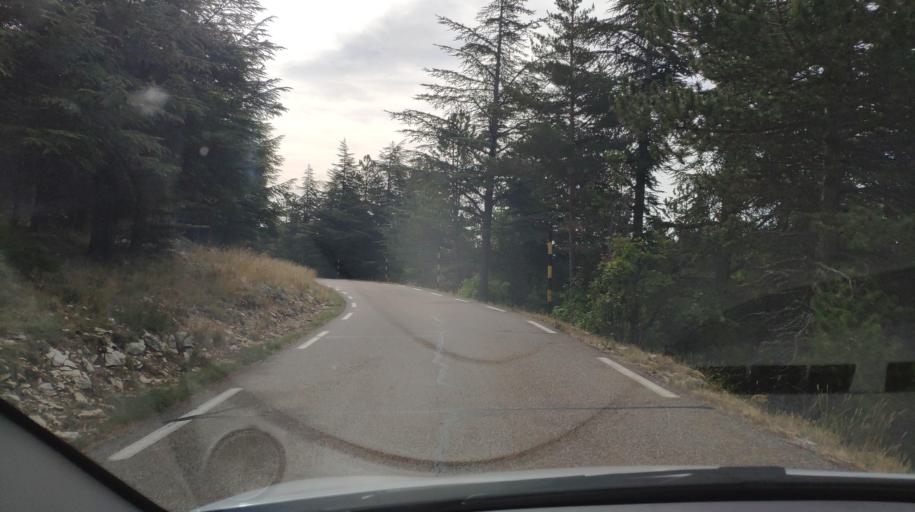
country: FR
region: Provence-Alpes-Cote d'Azur
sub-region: Departement du Vaucluse
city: Sault
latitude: 44.1464
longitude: 5.3599
